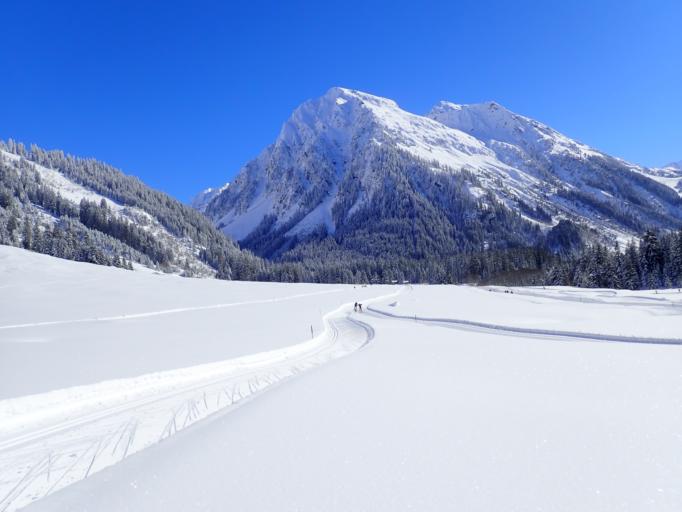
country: CH
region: Grisons
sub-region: Praettigau/Davos District
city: Klosters Serneus
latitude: 46.8577
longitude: 9.9489
